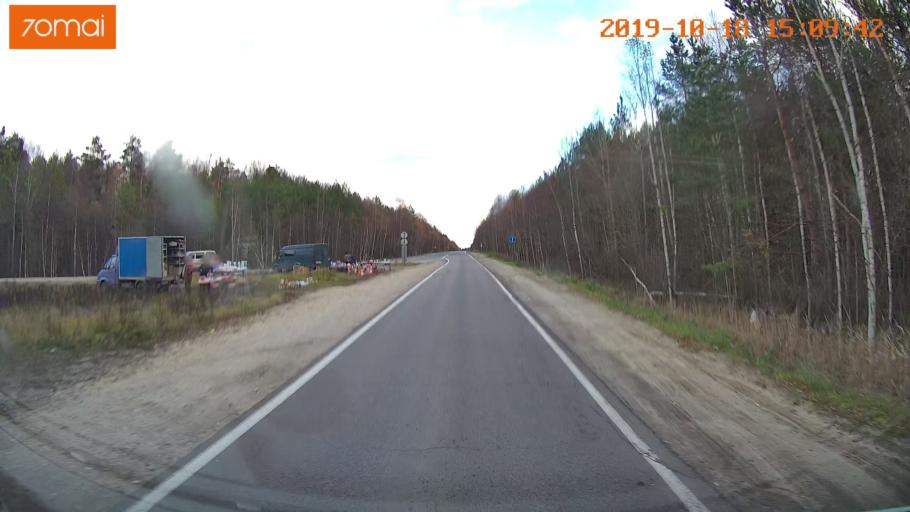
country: RU
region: Vladimir
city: Gus'-Khrustal'nyy
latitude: 55.5674
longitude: 40.6248
